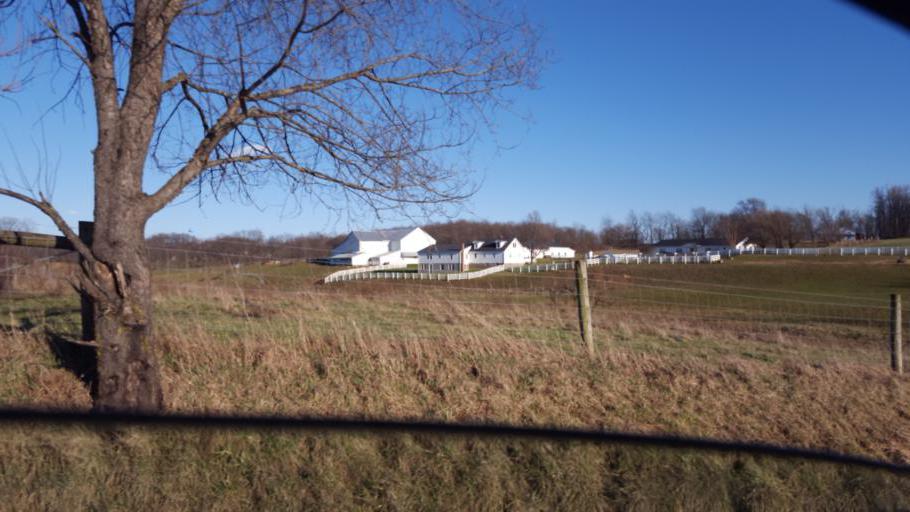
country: US
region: Ohio
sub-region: Tuscarawas County
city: Sugarcreek
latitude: 40.6013
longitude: -81.7614
